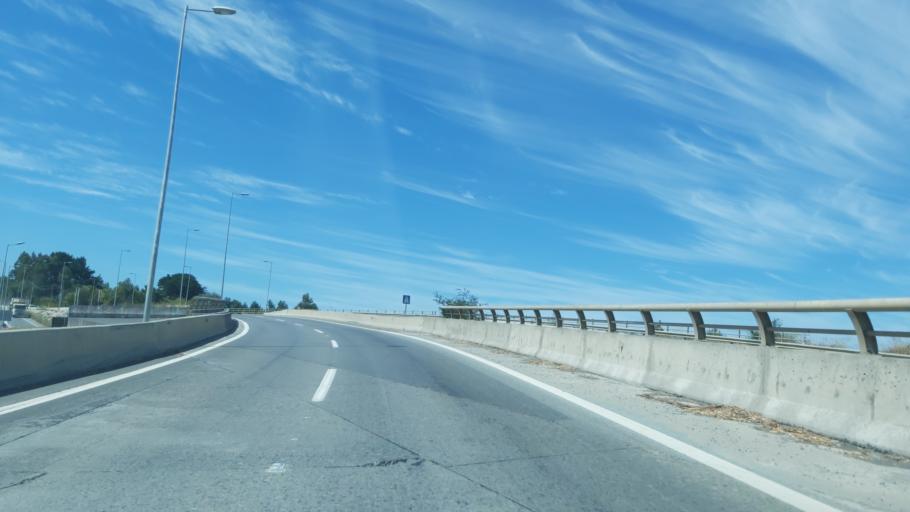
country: CL
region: Biobio
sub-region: Provincia de Concepcion
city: Coronel
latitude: -37.0471
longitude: -73.1426
